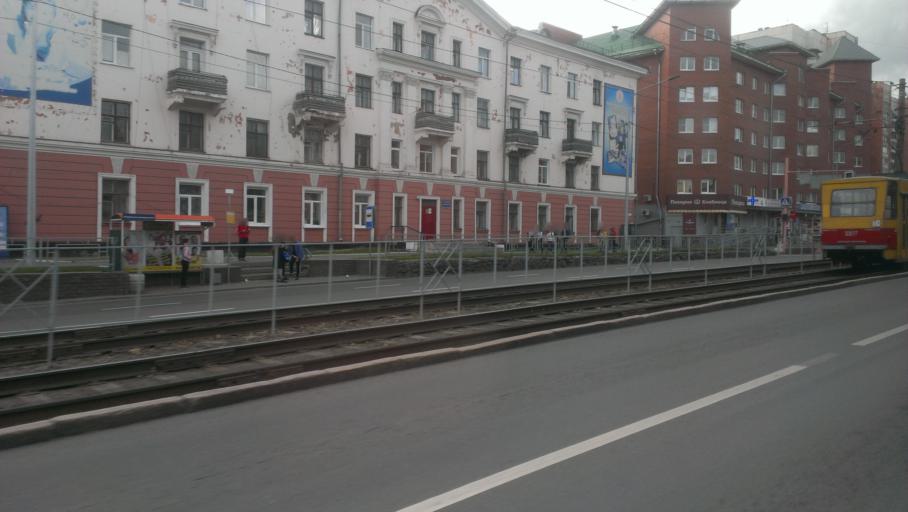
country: RU
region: Altai Krai
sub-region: Gorod Barnaulskiy
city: Barnaul
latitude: 53.3420
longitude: 83.7698
